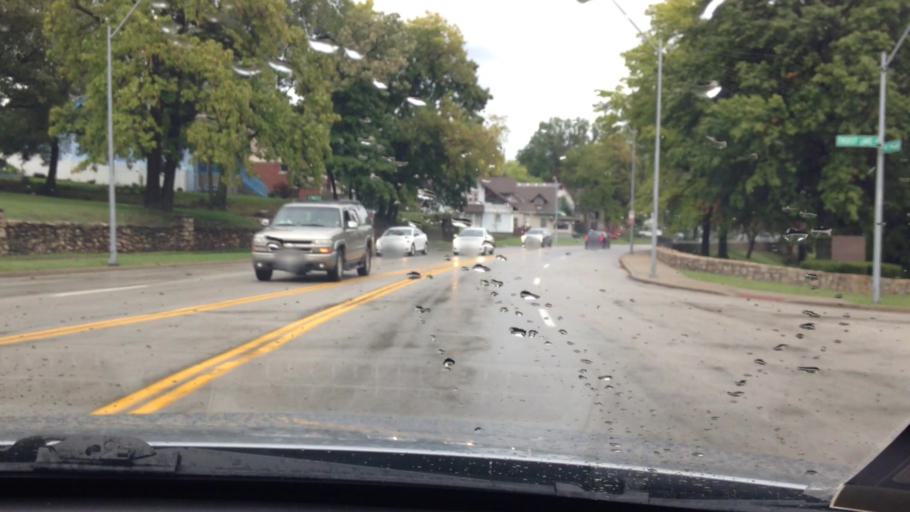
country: US
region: Missouri
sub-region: Jackson County
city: Kansas City
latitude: 39.0741
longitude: -94.5666
